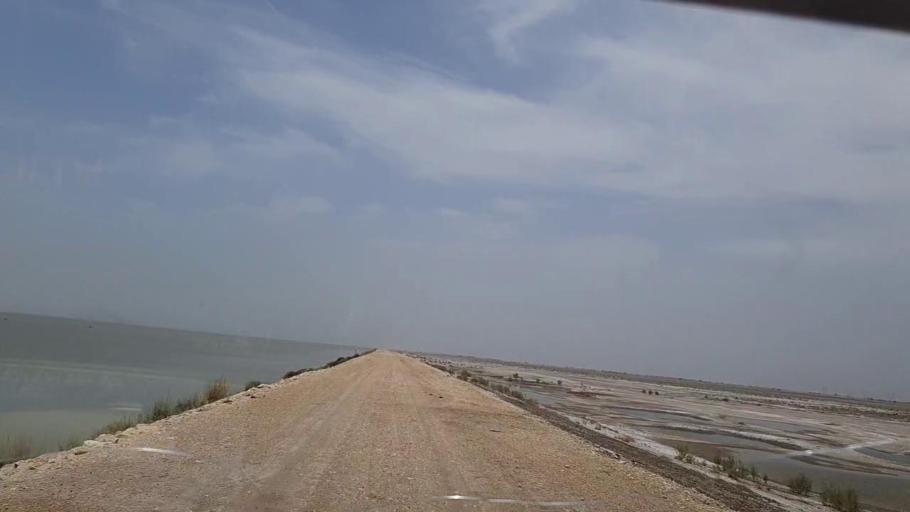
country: PK
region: Sindh
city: Sehwan
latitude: 26.4117
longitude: 67.7900
